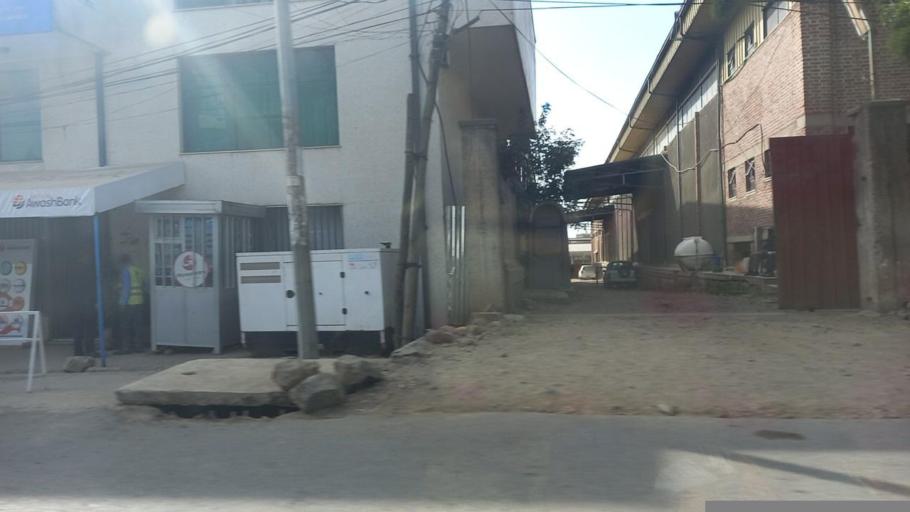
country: ET
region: Adis Abeba
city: Addis Ababa
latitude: 9.0073
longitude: 38.8197
